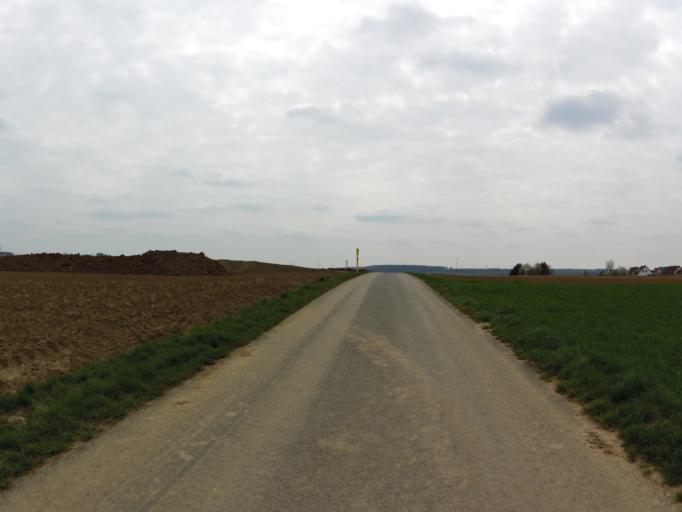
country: DE
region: Bavaria
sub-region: Regierungsbezirk Unterfranken
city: Rottendorf
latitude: 49.8033
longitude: 10.0282
